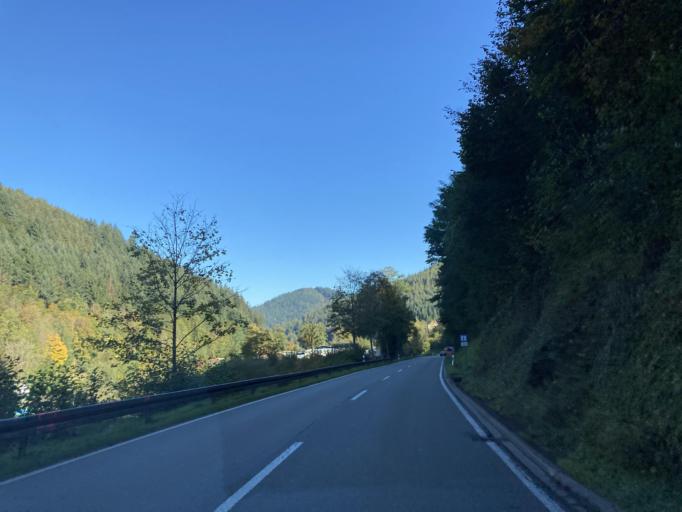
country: DE
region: Baden-Wuerttemberg
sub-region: Freiburg Region
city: Hornberg
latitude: 48.1953
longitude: 8.2333
